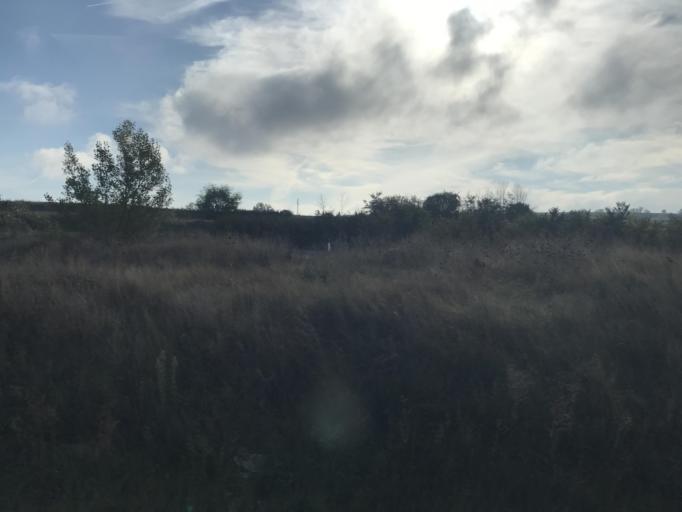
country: ES
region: Castille and Leon
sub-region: Provincia de Burgos
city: Briviesca
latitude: 42.5676
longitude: -3.3074
